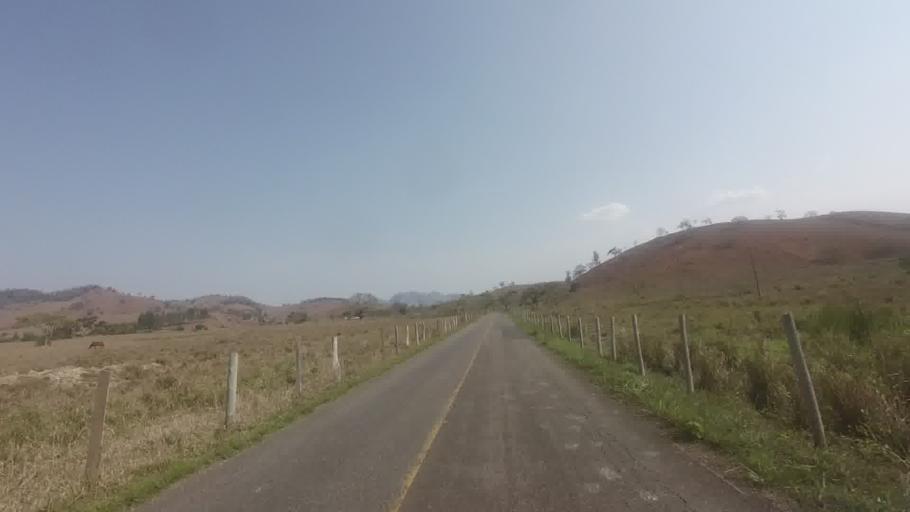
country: BR
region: Rio de Janeiro
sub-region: Bom Jesus Do Itabapoana
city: Bom Jesus do Itabapoana
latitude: -21.1307
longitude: -41.5679
